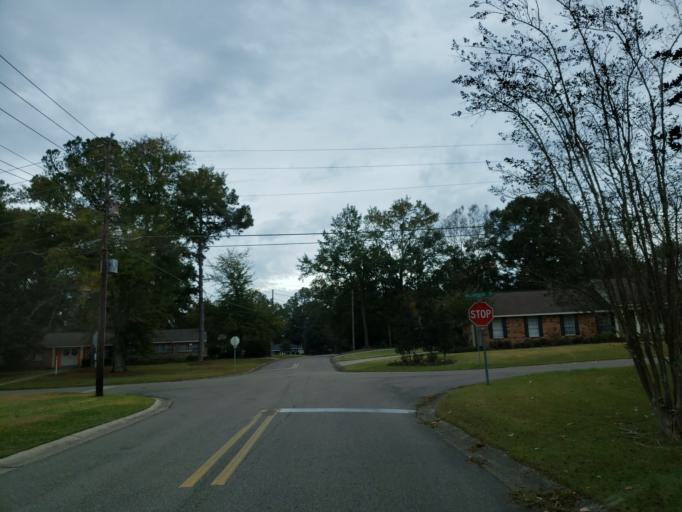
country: US
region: Mississippi
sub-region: Lamar County
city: West Hattiesburg
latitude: 31.3122
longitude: -89.3346
